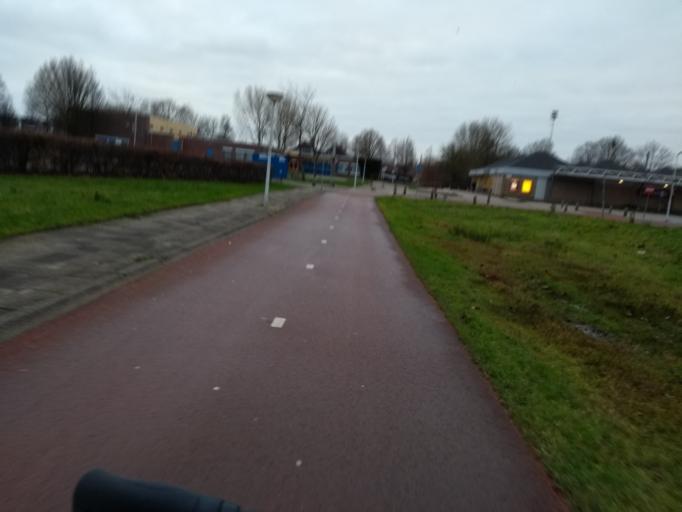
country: NL
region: Friesland
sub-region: Sudwest Fryslan
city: Sneek
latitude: 53.0219
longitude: 5.6480
